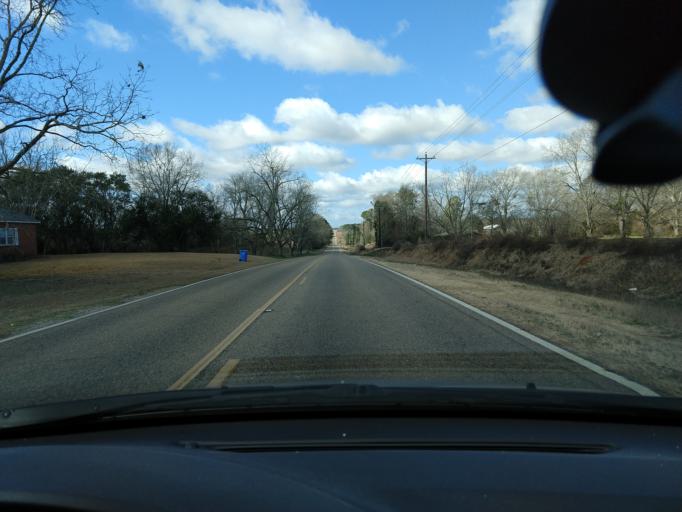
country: US
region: Alabama
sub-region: Coffee County
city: New Brockton
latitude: 31.3128
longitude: -85.9546
